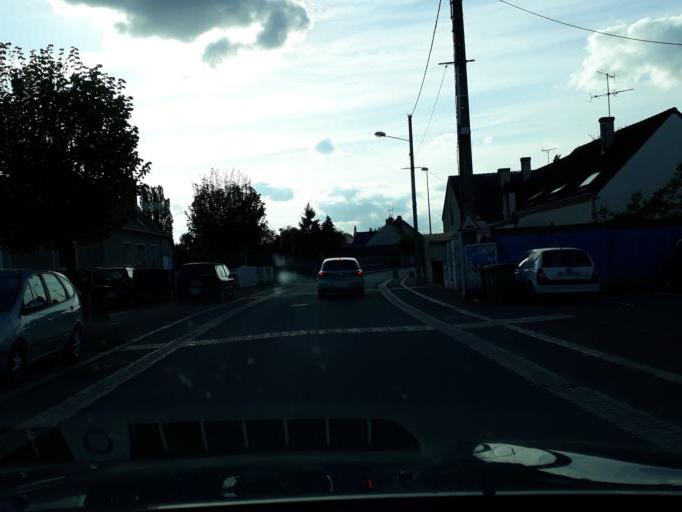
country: FR
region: Centre
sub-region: Departement du Loiret
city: Saint-Jean-de-la-Ruelle
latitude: 47.9205
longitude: 1.8755
